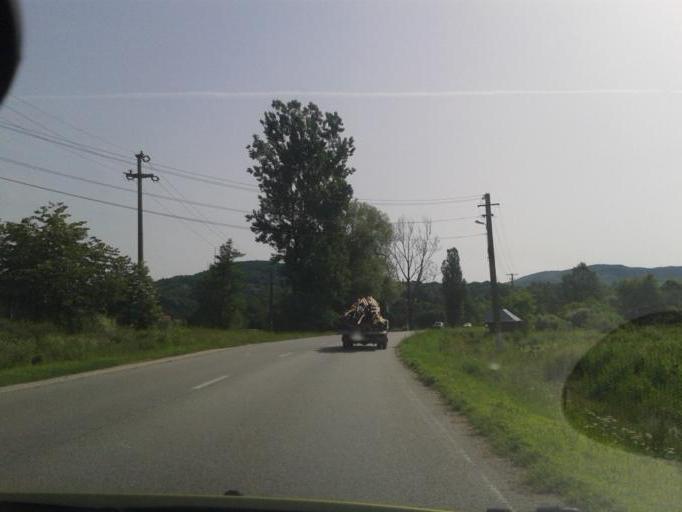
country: RO
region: Valcea
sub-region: Comuna Stoenesti
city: Stoenesti
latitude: 45.1140
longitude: 24.1627
